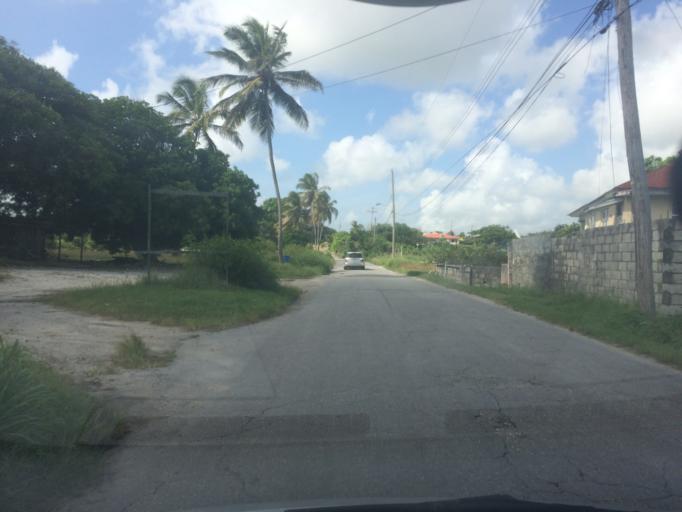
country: BB
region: Christ Church
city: Oistins
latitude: 13.0735
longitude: -59.5106
